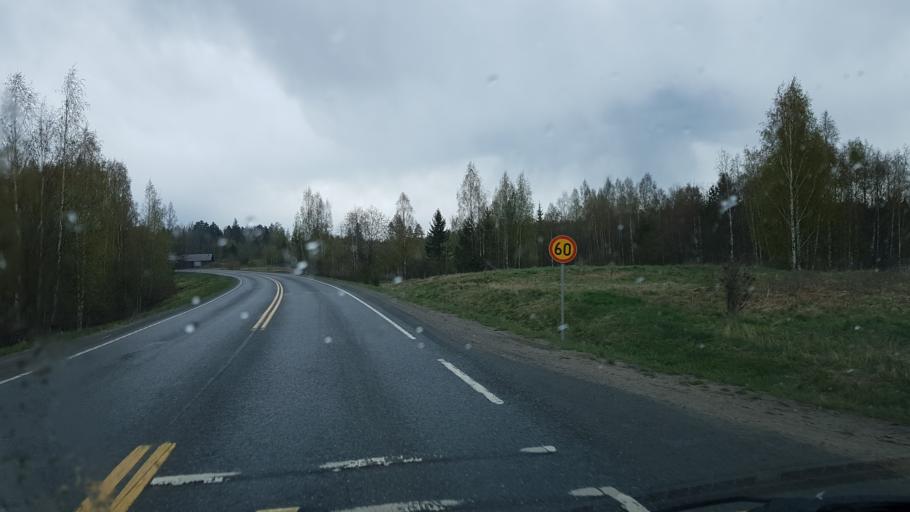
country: FI
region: Pirkanmaa
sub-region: Tampere
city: Pirkkala
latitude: 61.4235
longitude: 23.6346
